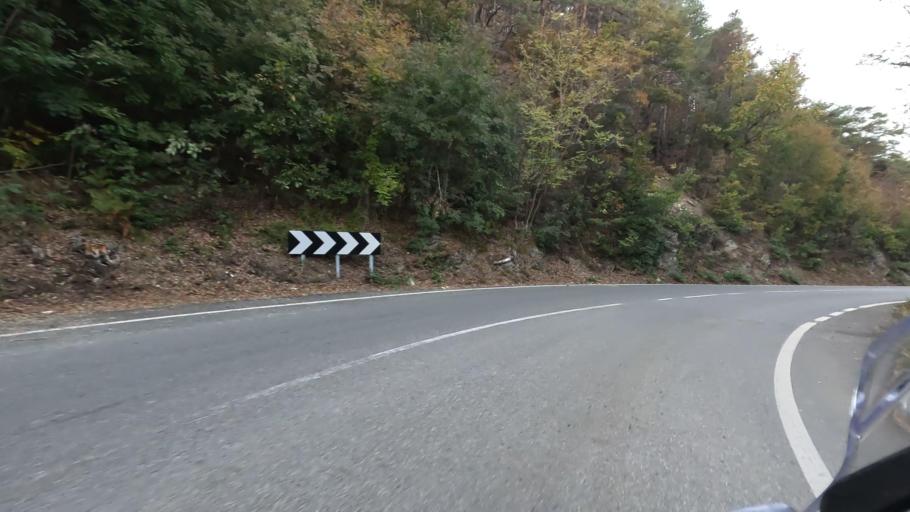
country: IT
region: Liguria
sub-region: Provincia di Savona
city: Sassello
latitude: 44.5066
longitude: 8.4822
